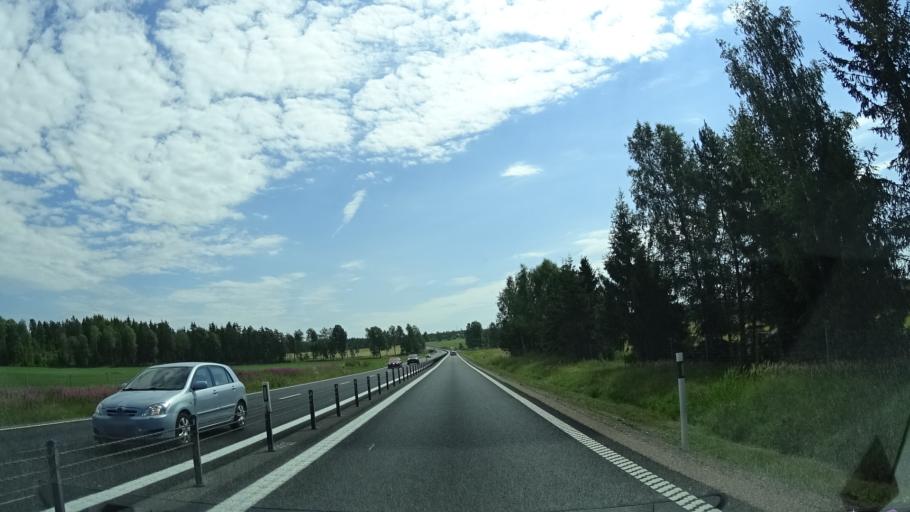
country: SE
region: Vaermland
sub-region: Karlstads Kommun
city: Skattkarr
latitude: 59.3974
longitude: 13.8056
